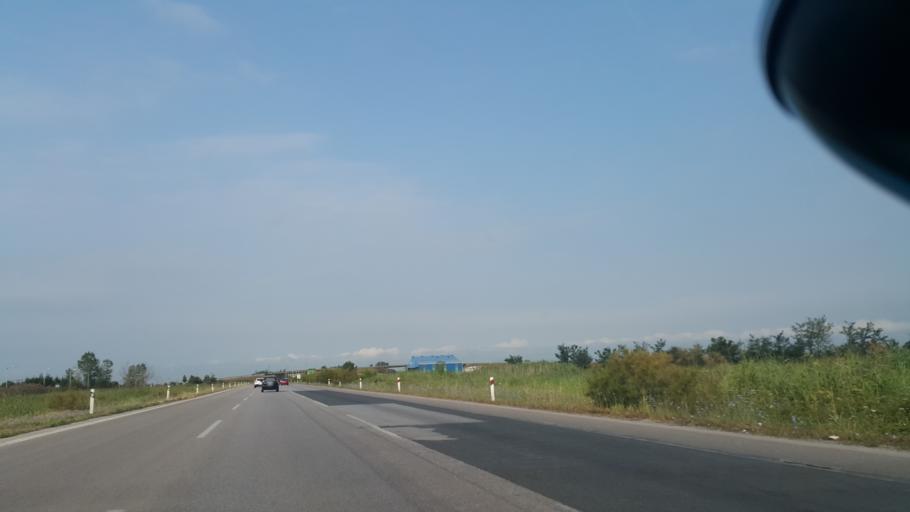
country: GR
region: Central Macedonia
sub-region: Nomos Thessalonikis
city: Chalastra
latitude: 40.6132
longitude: 22.7408
